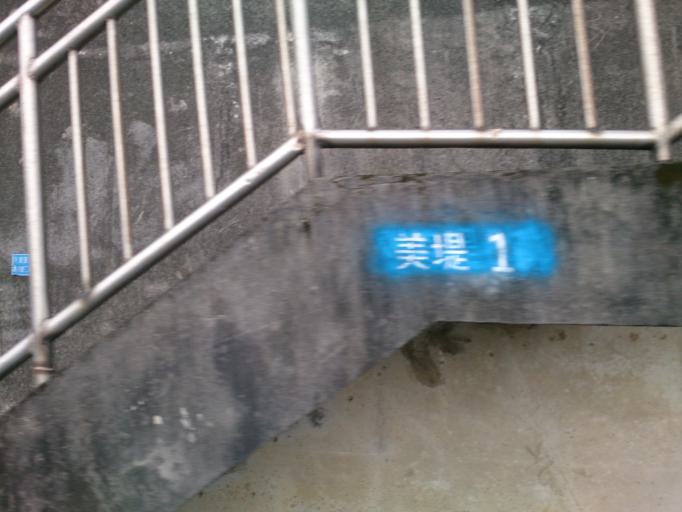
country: TW
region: Taipei
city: Taipei
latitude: 25.0730
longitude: 121.5729
